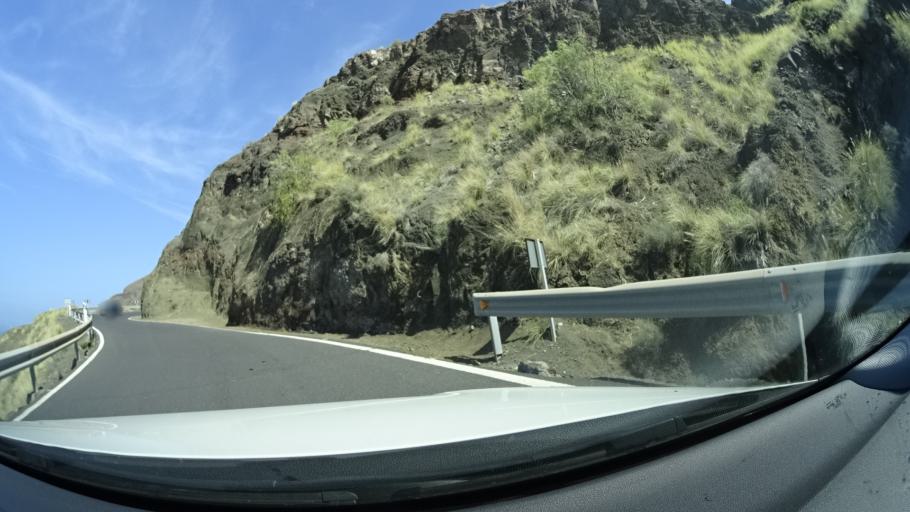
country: ES
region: Canary Islands
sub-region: Provincia de Las Palmas
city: Agaete
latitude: 28.0863
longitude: -15.7045
